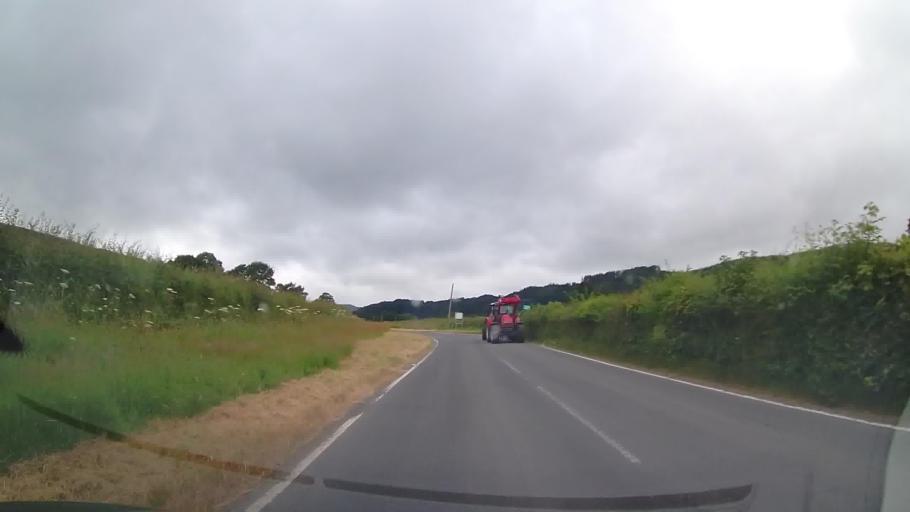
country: GB
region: Wales
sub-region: Denbighshire
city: Llandrillo
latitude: 52.9248
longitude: -3.4485
